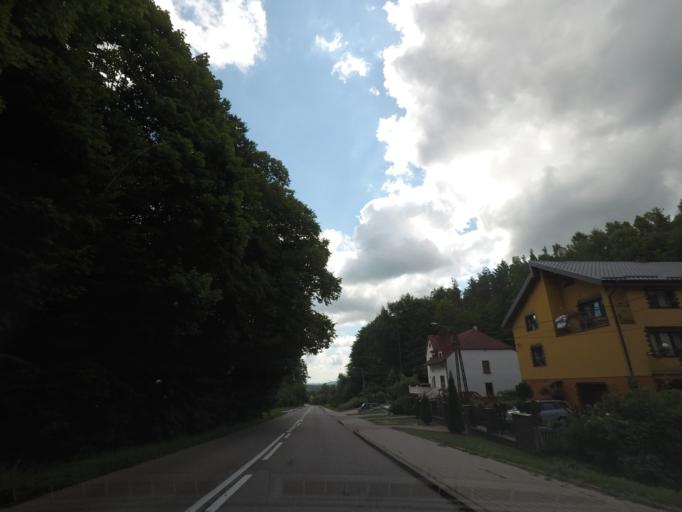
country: PL
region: Pomeranian Voivodeship
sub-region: Powiat wejherowski
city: Leczyce
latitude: 54.5958
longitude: 17.8508
